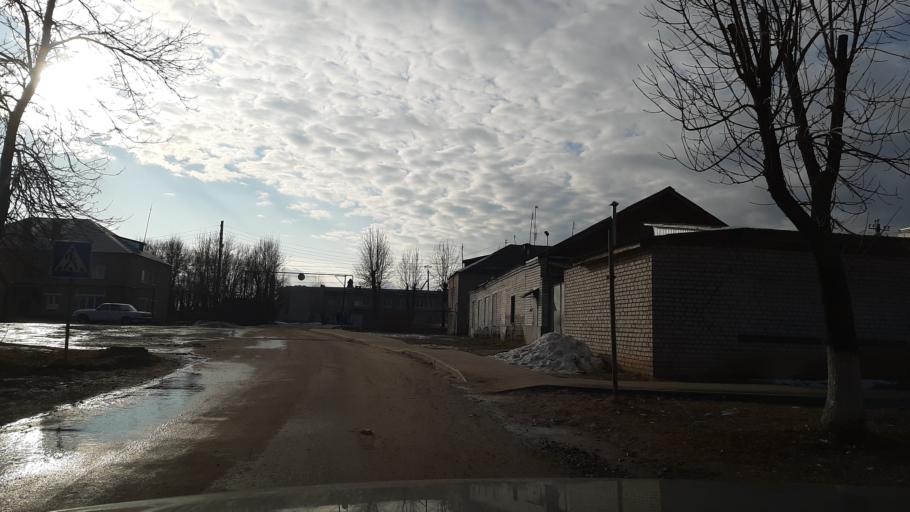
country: RU
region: Ivanovo
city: Novo-Talitsy
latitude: 56.9216
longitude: 40.7367
